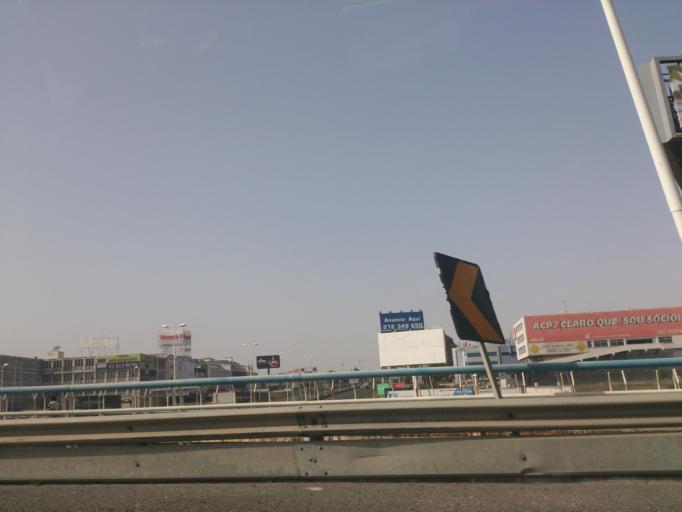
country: PT
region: Lisbon
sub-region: Loures
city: Sacavem
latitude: 38.7891
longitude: -9.1161
